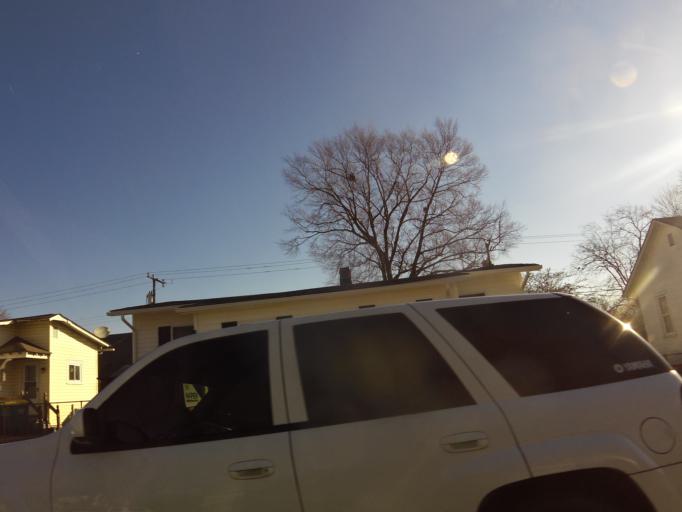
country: US
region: Virginia
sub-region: City of Hopewell
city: Hopewell
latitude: 37.3043
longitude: -77.2920
